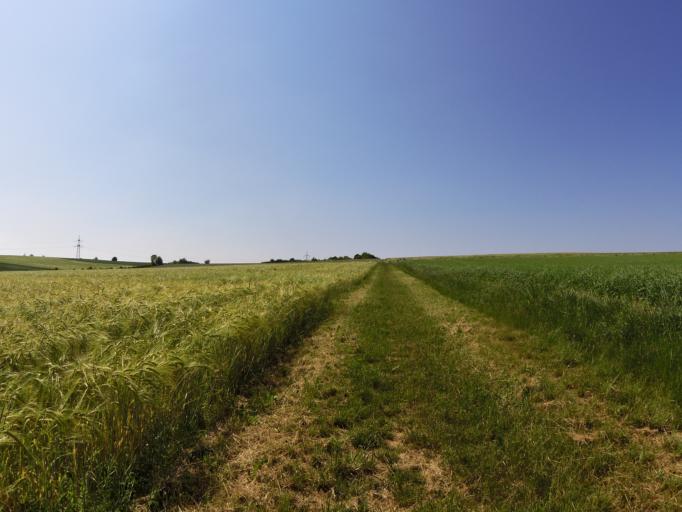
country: DE
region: Bavaria
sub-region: Regierungsbezirk Unterfranken
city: Kleinrinderfeld
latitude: 49.7100
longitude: 9.8555
